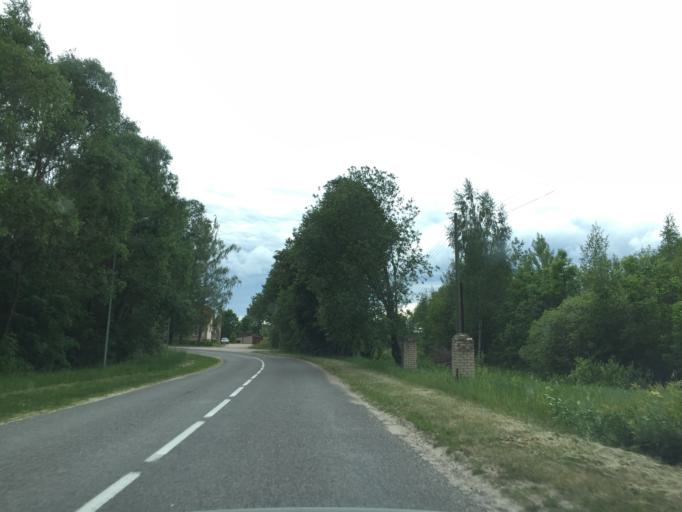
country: LV
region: Vilanu
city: Vilani
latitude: 56.4446
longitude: 27.0879
